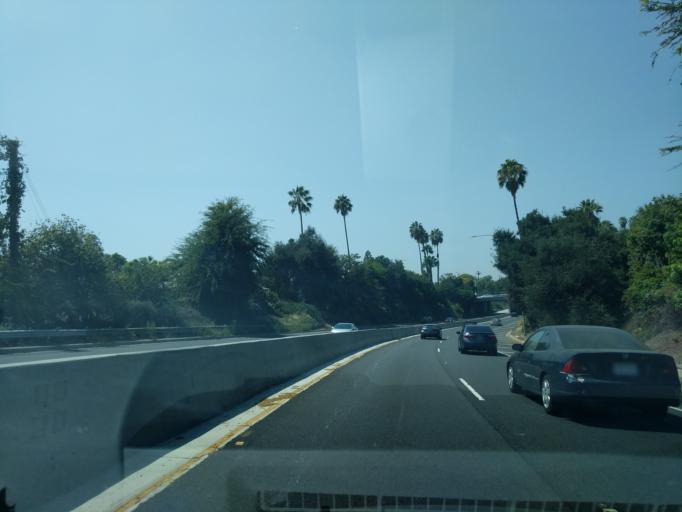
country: US
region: California
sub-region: Los Angeles County
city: South Pasadena
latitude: 34.1195
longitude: -118.1481
